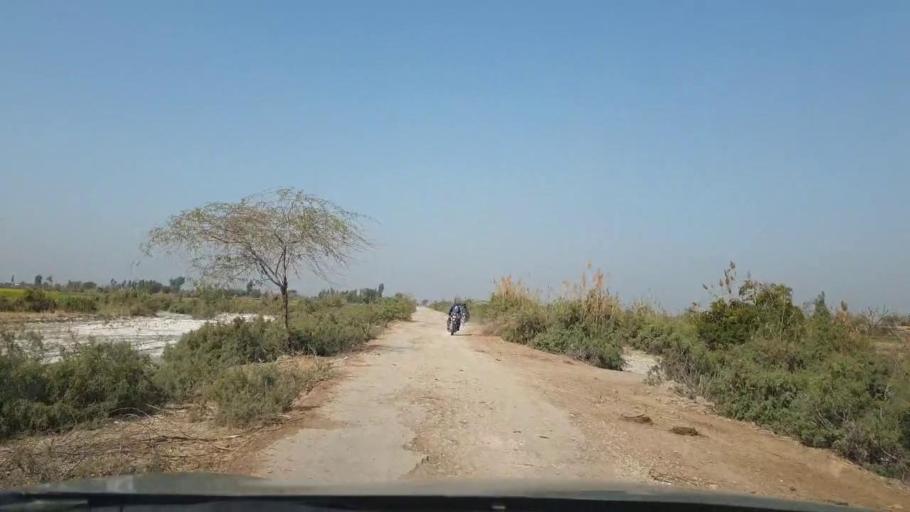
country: PK
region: Sindh
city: Berani
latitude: 25.6809
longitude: 68.8941
